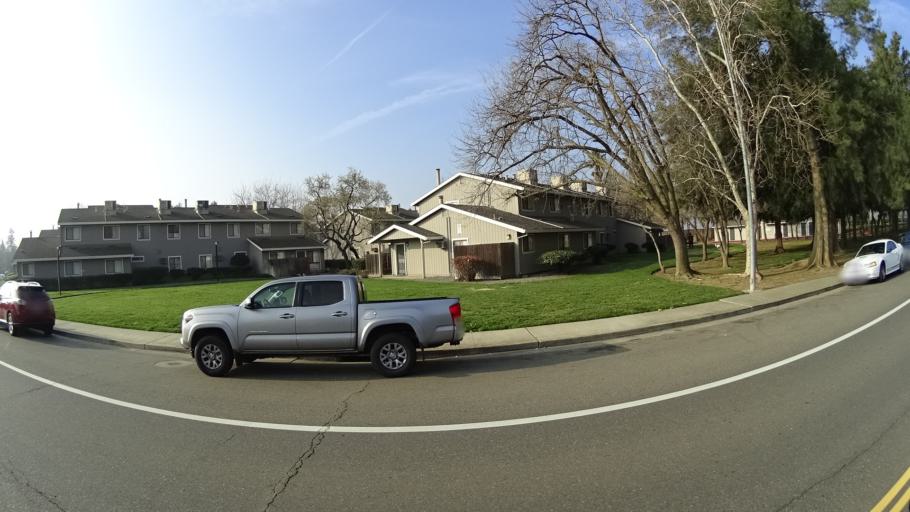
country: US
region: California
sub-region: Yolo County
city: Davis
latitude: 38.5670
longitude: -121.7660
